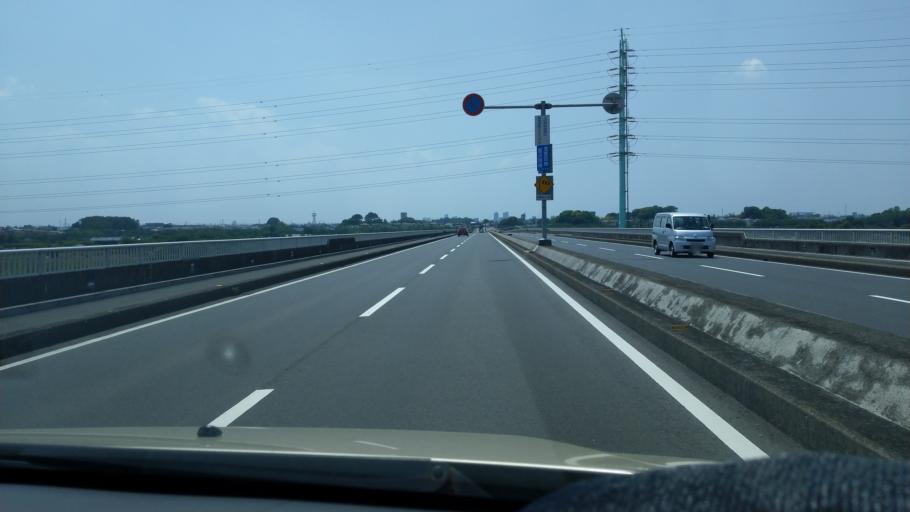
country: JP
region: Saitama
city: Saitama
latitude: 35.8864
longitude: 139.7041
